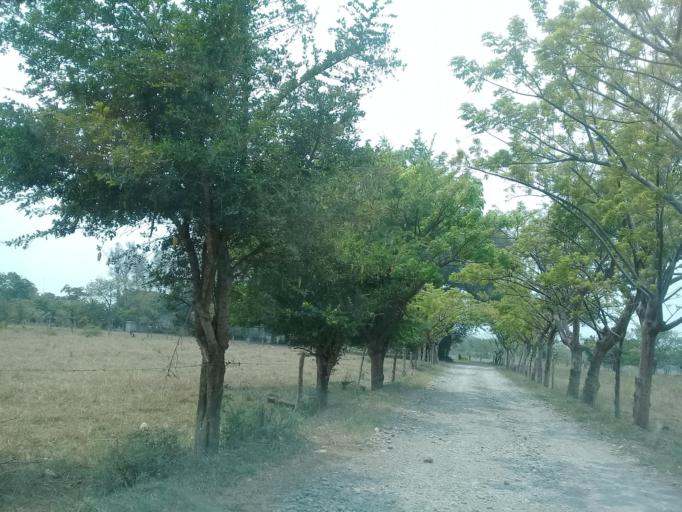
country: MX
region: Veracruz
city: Jamapa
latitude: 18.9328
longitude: -96.2136
